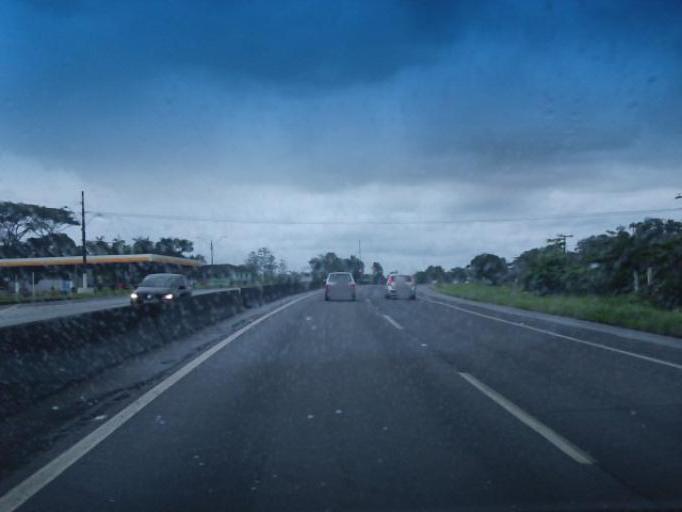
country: BR
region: Santa Catarina
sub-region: Barra Velha
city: Barra Velha
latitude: -26.5548
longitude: -48.7199
